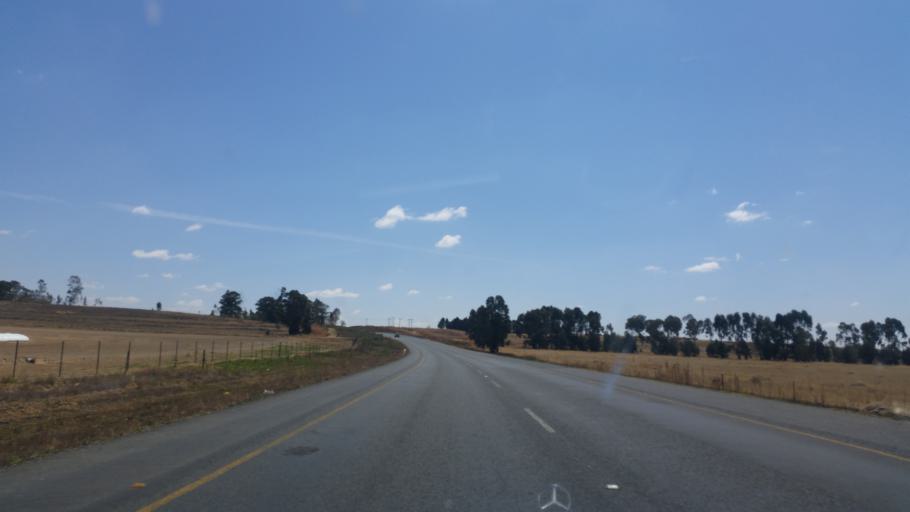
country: ZA
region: Orange Free State
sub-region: Thabo Mofutsanyana District Municipality
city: Bethlehem
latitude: -28.1179
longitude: 28.6797
